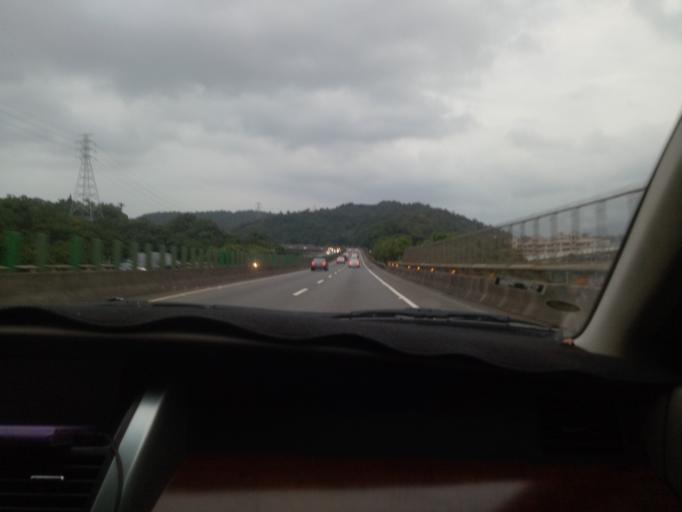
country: TW
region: Taiwan
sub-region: Keelung
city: Keelung
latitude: 25.1031
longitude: 121.7561
